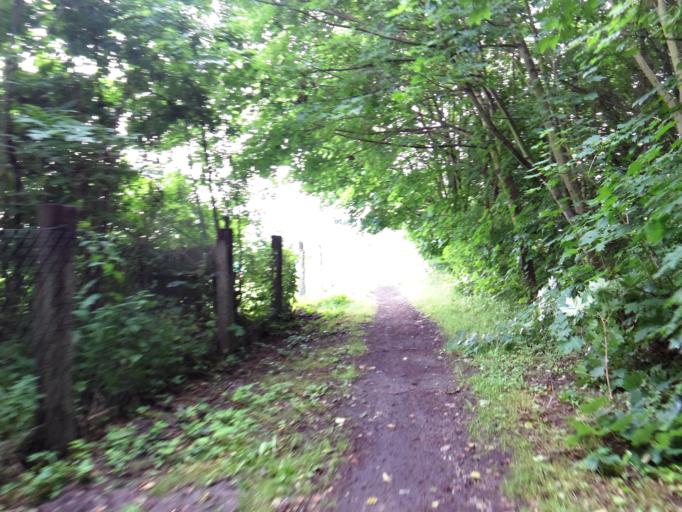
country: DE
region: Saxony
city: Taucha
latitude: 51.3442
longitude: 12.4862
